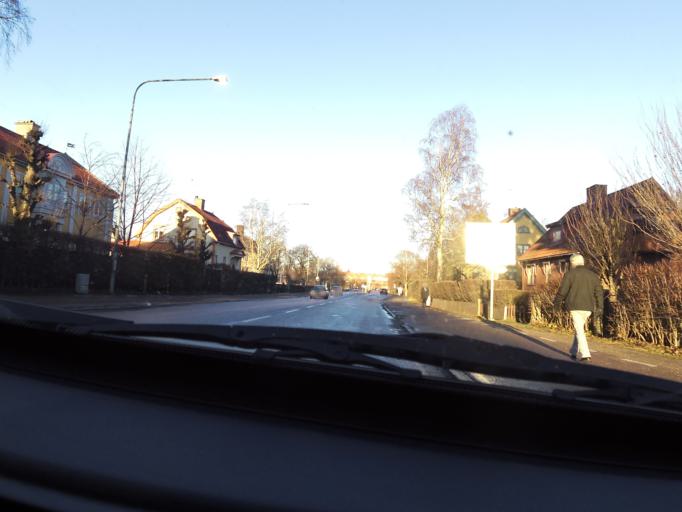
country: SE
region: Gaevleborg
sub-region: Gavle Kommun
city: Gavle
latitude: 60.6701
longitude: 17.1344
